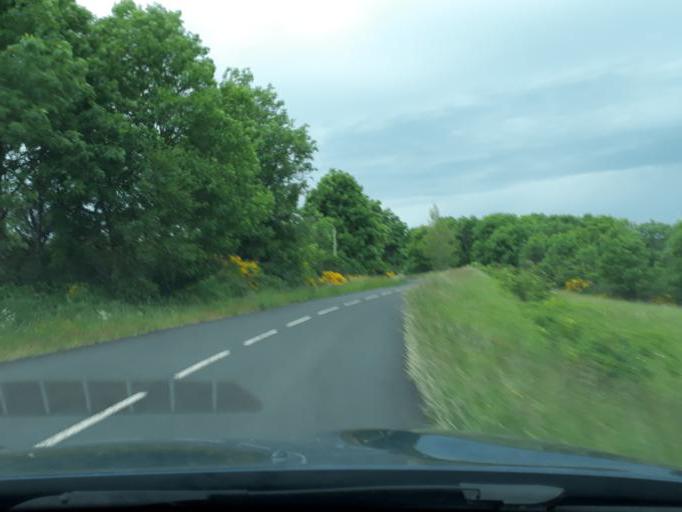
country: FR
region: Languedoc-Roussillon
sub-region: Departement de l'Herault
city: Lodeve
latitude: 43.8352
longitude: 3.2612
